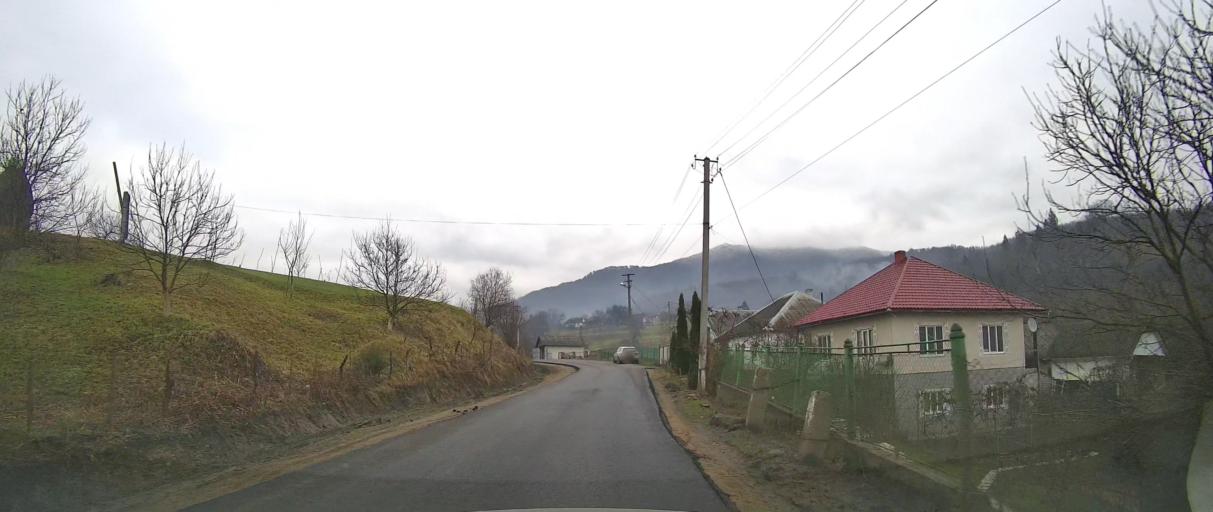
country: UA
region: Zakarpattia
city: Velykyi Bereznyi
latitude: 48.9617
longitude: 22.5490
